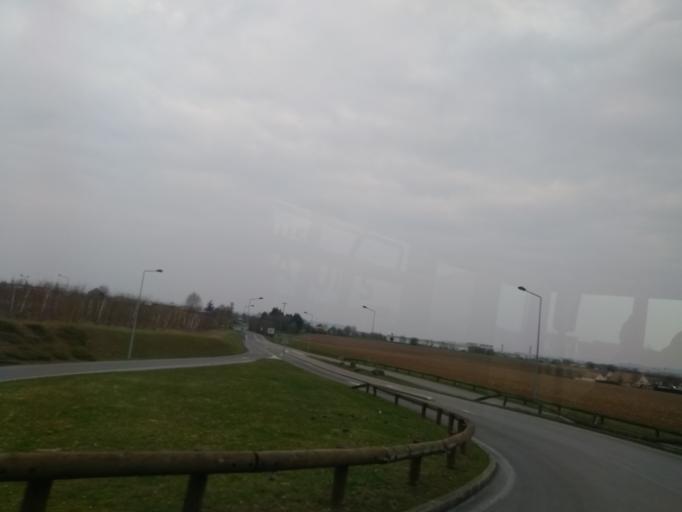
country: FR
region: Picardie
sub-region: Departement de l'Oise
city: Jaux
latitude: 49.4012
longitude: 2.7754
